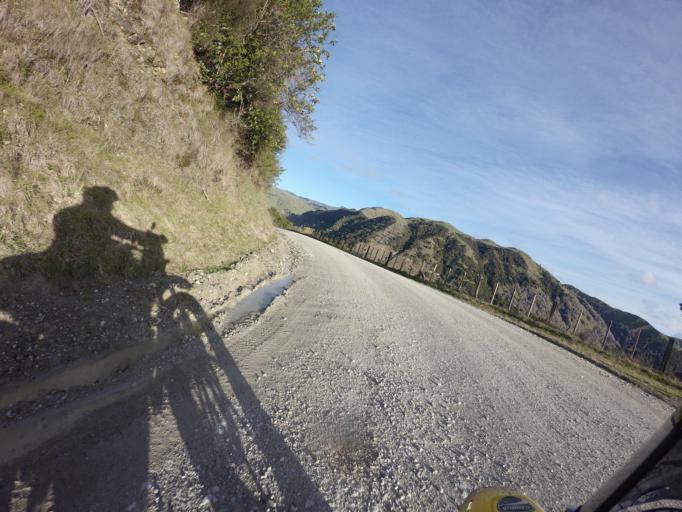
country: NZ
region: Hawke's Bay
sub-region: Wairoa District
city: Wairoa
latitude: -38.7202
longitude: 177.5794
